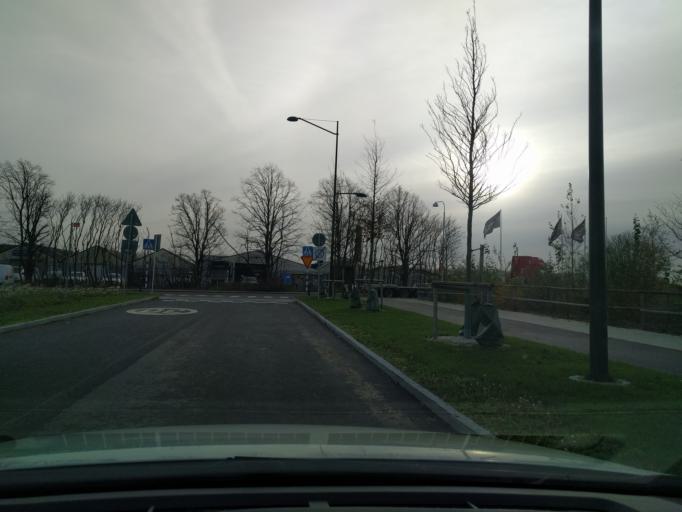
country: SE
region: Skane
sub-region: Malmo
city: Bunkeflostrand
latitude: 55.5586
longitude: 12.9821
